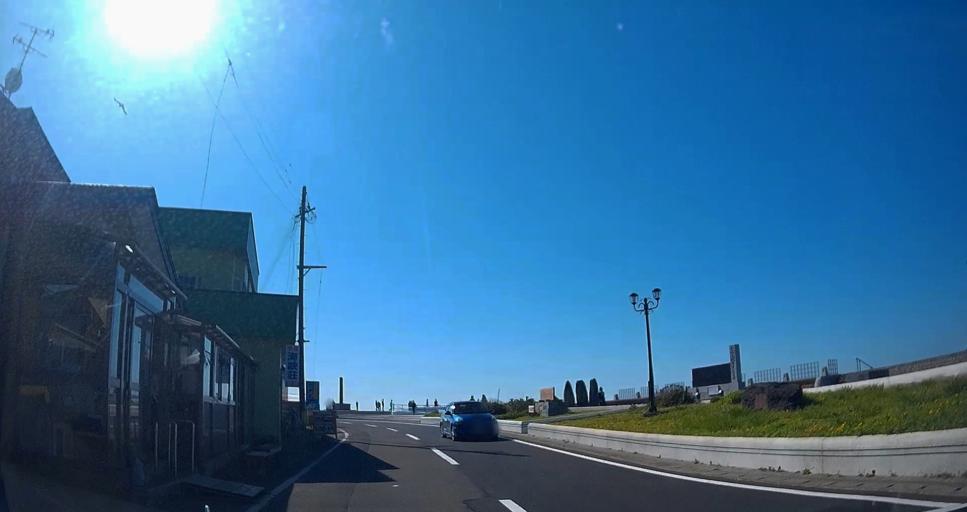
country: JP
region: Hokkaido
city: Hakodate
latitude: 41.5462
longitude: 140.9137
